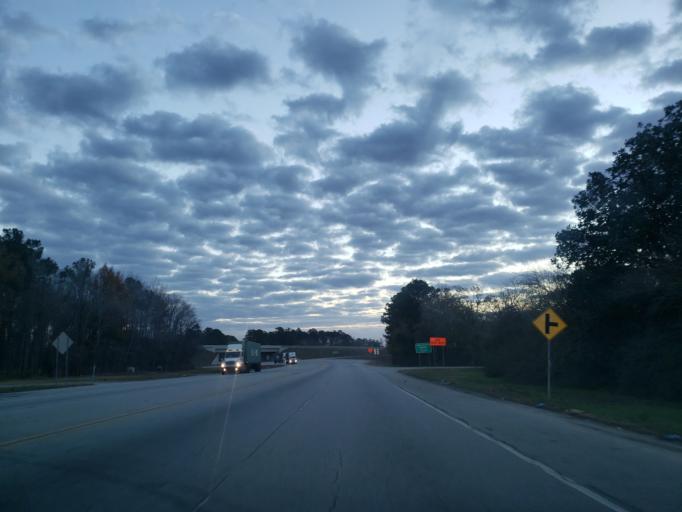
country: US
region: Georgia
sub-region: Chatham County
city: Port Wentworth
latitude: 32.1619
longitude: -81.1819
